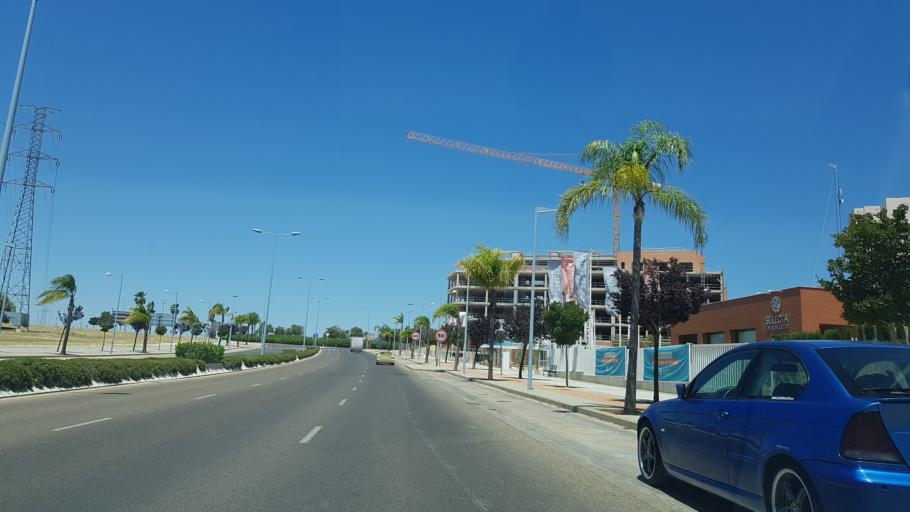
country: ES
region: Andalusia
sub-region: Provincia de Sevilla
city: Dos Hermanas
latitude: 37.3189
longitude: -5.9409
